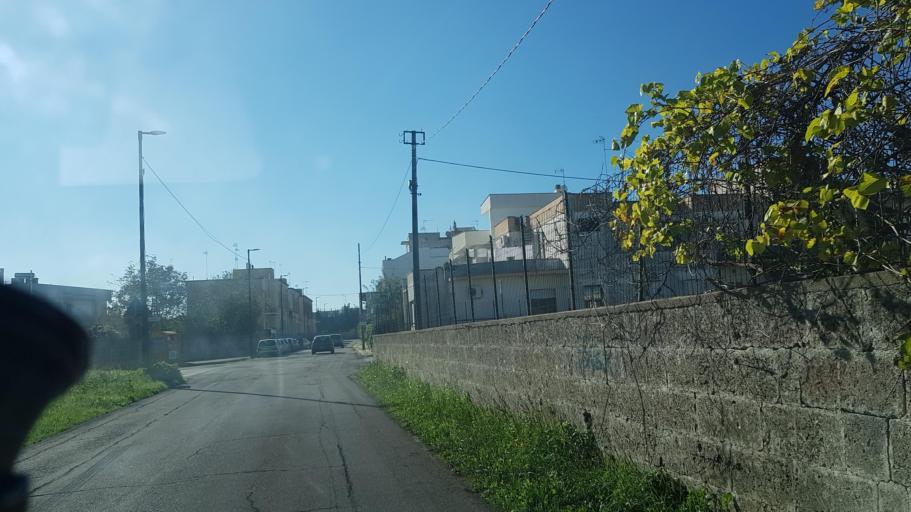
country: IT
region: Apulia
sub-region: Provincia di Lecce
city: Arnesano
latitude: 40.3400
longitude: 18.0900
